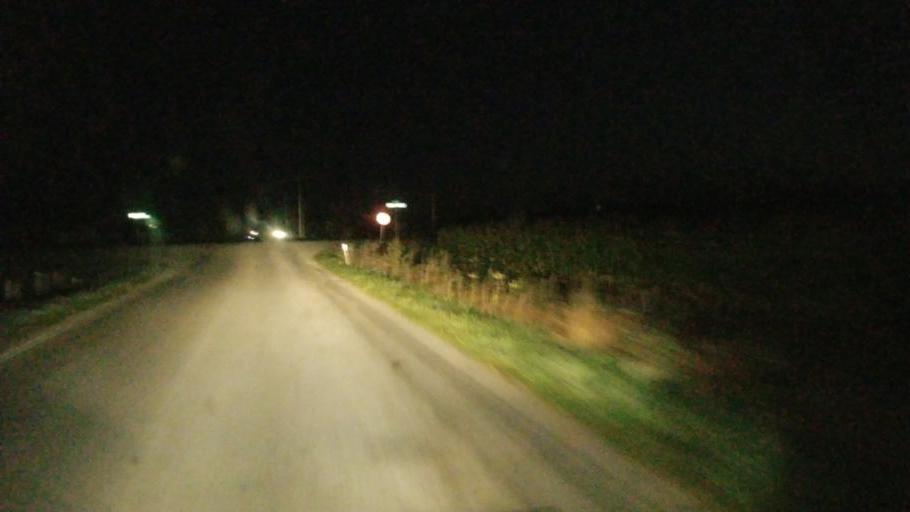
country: US
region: Indiana
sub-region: Elkhart County
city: Middlebury
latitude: 41.6754
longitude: -85.6196
